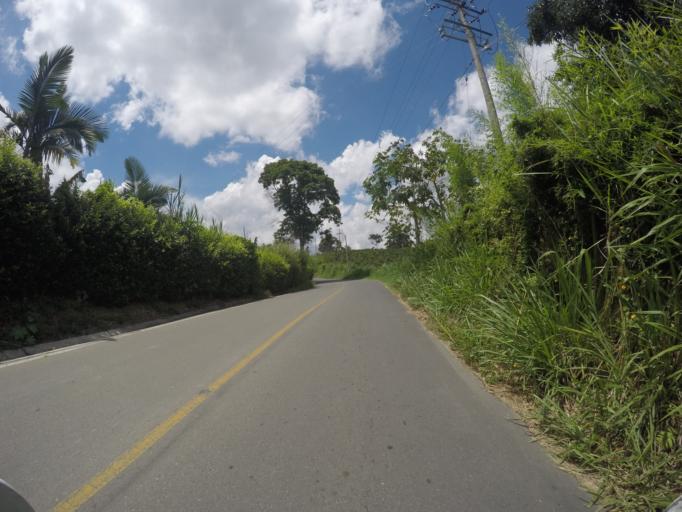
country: CO
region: Quindio
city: Quimbaya
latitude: 4.6243
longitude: -75.7512
